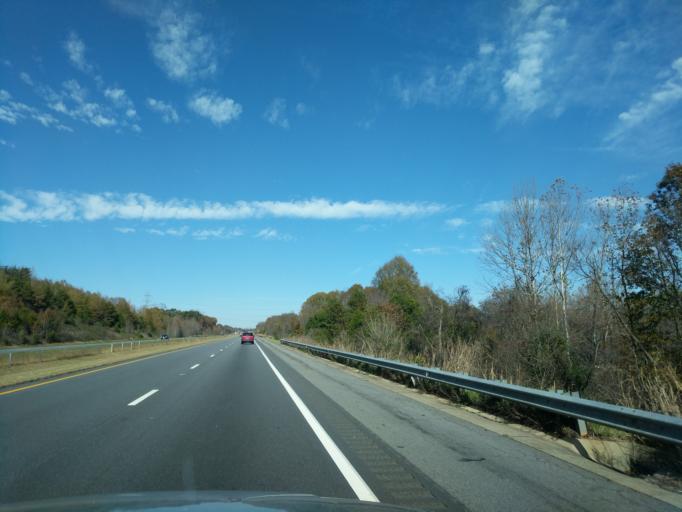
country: US
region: North Carolina
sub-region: Catawba County
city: Maiden
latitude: 35.5626
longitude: -81.2477
